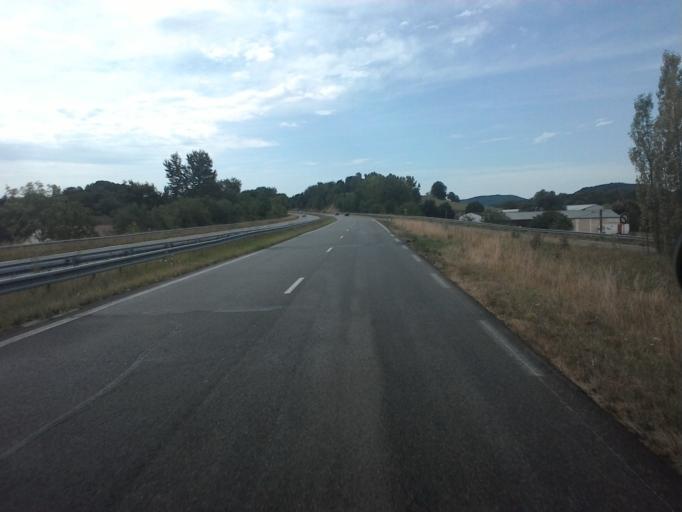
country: FR
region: Franche-Comte
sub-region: Departement du Jura
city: Montmorot
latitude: 46.7594
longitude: 5.5564
